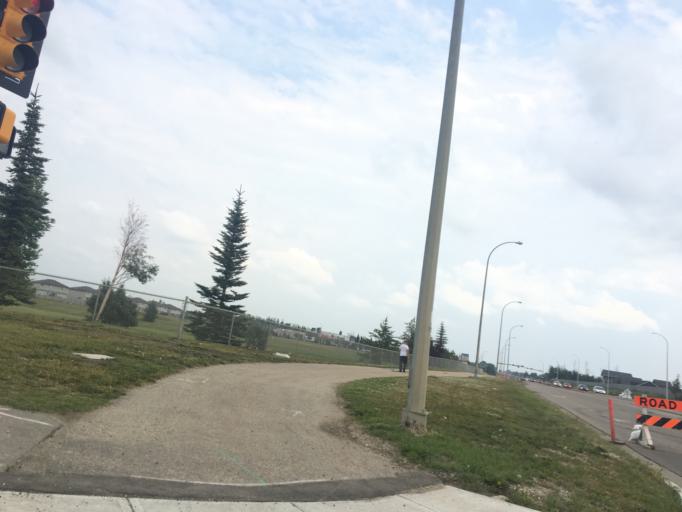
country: CA
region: Alberta
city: Grande Prairie
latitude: 55.1418
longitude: -118.8076
